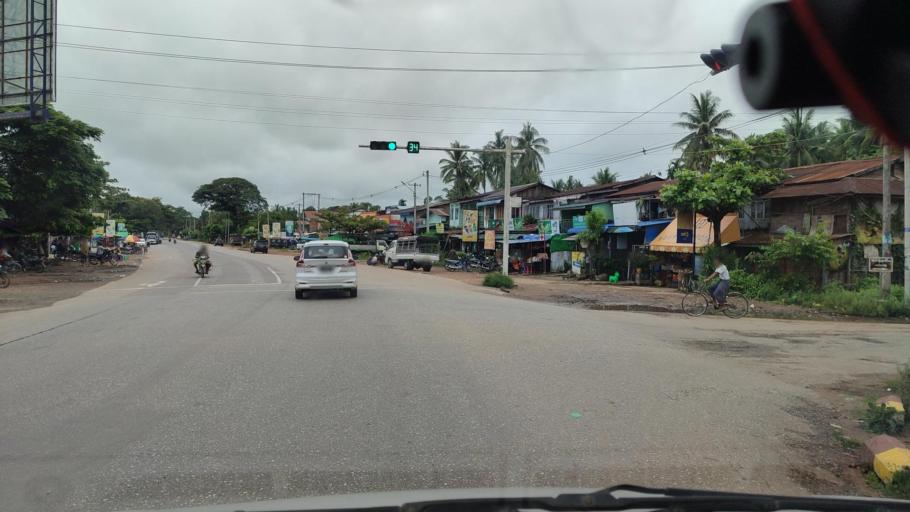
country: MM
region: Bago
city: Letpandan
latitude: 17.7897
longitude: 95.7731
